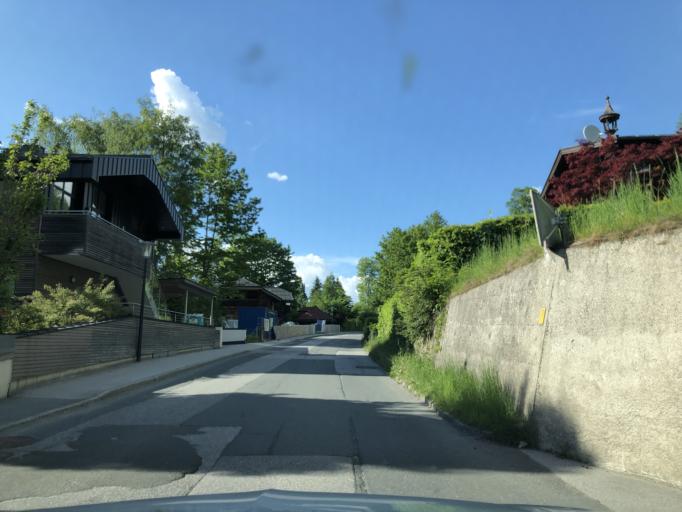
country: AT
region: Salzburg
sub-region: Politischer Bezirk Zell am See
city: Zell am See
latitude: 47.3244
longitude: 12.8160
